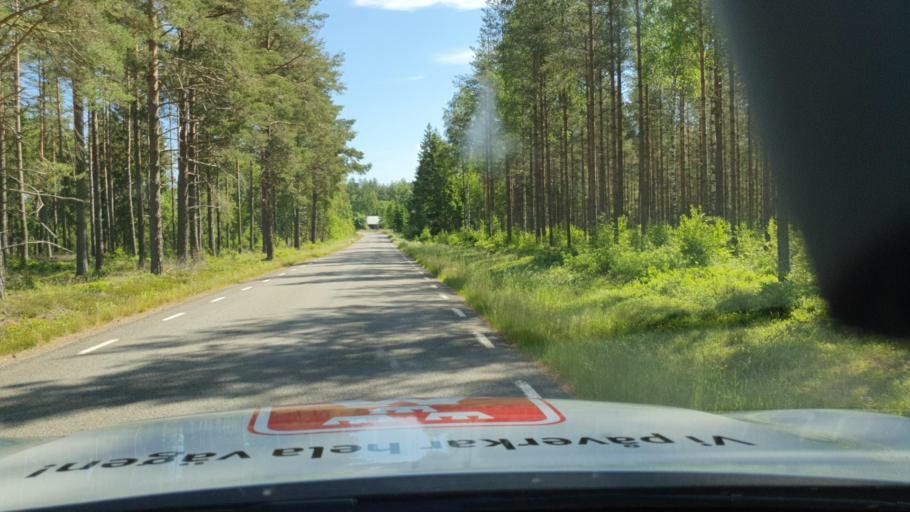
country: SE
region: Vaestra Goetaland
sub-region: Tidaholms Kommun
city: Olofstorp
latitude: 58.2763
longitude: 13.9671
